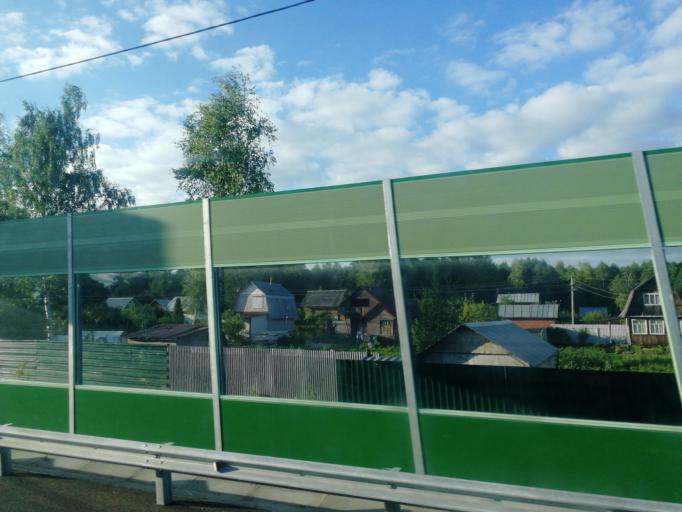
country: RU
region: Kaluga
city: Kaluga
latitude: 54.4553
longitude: 36.2862
